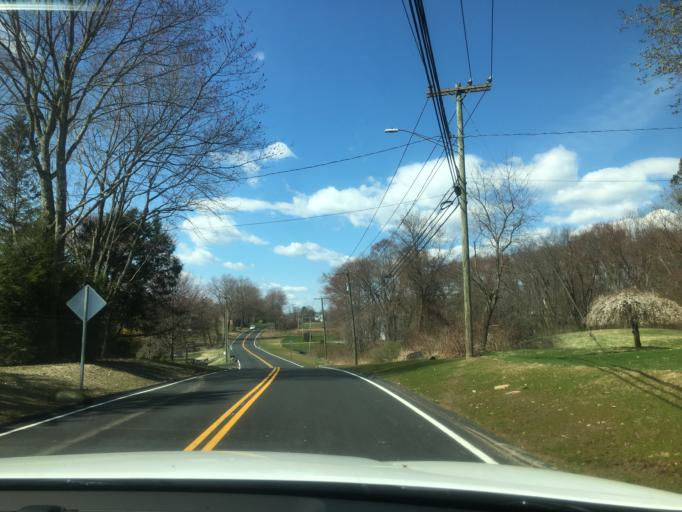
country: US
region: Connecticut
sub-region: Hartford County
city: Hazardville
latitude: 41.9586
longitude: -72.5326
